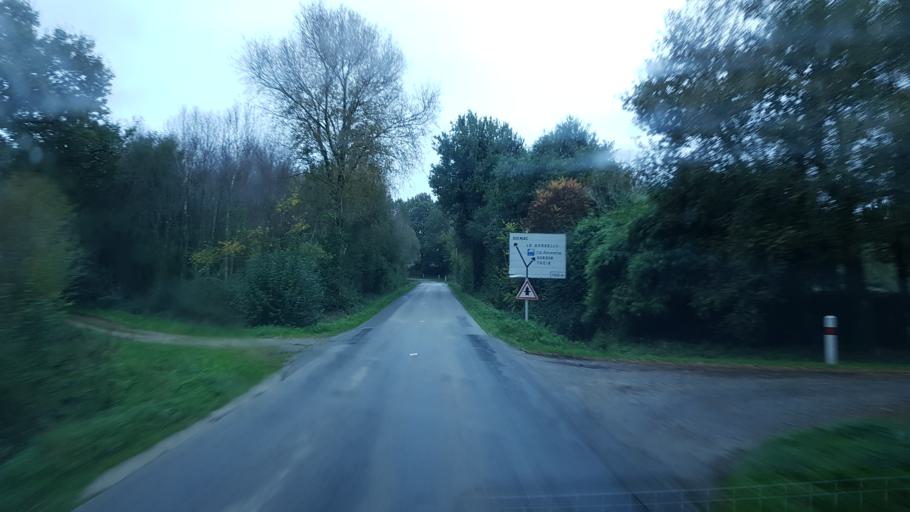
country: FR
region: Brittany
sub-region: Departement du Morbihan
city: Sulniac
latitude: 47.6828
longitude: -2.5714
